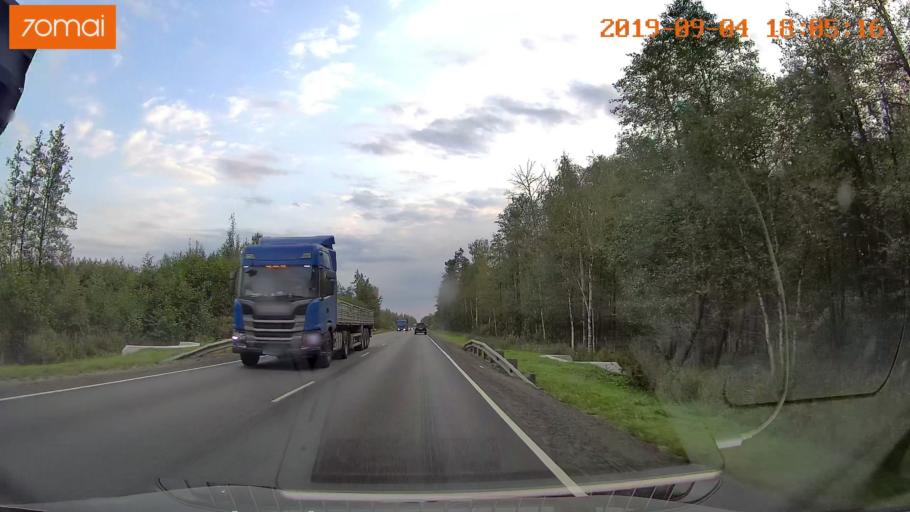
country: RU
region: Moskovskaya
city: Il'inskiy Pogost
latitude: 55.4433
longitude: 38.8288
